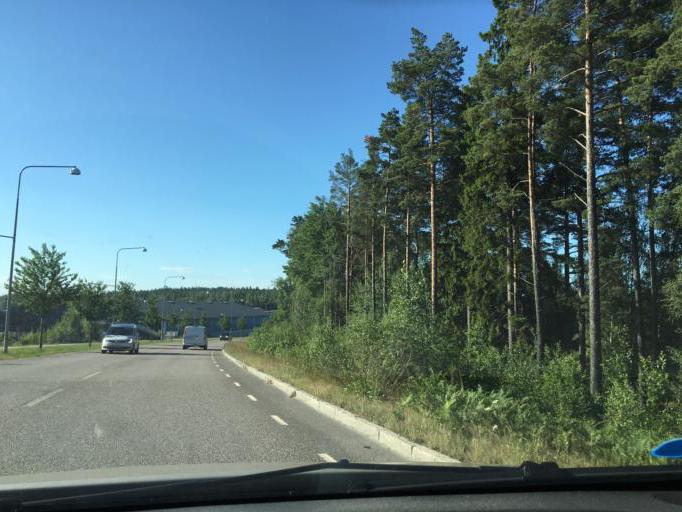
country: SE
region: Stockholm
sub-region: Sodertalje Kommun
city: Soedertaelje
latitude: 59.2052
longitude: 17.6643
